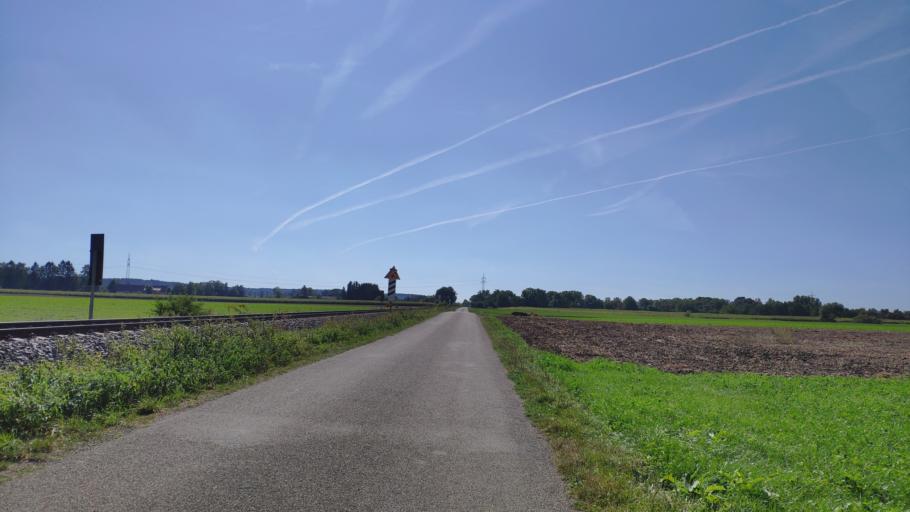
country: DE
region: Bavaria
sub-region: Swabia
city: Neu-Ulm
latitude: 48.3723
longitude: 10.0312
